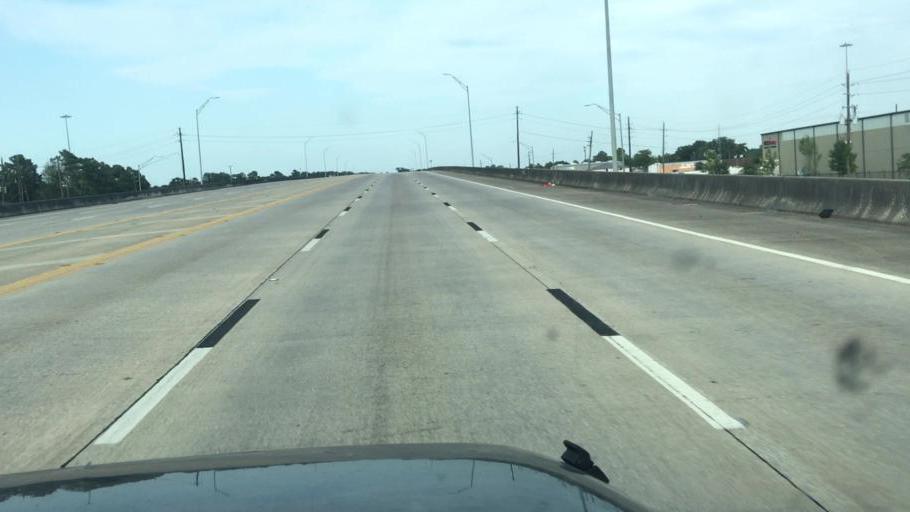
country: US
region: Texas
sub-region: Harris County
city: Spring
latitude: 30.0258
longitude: -95.4085
